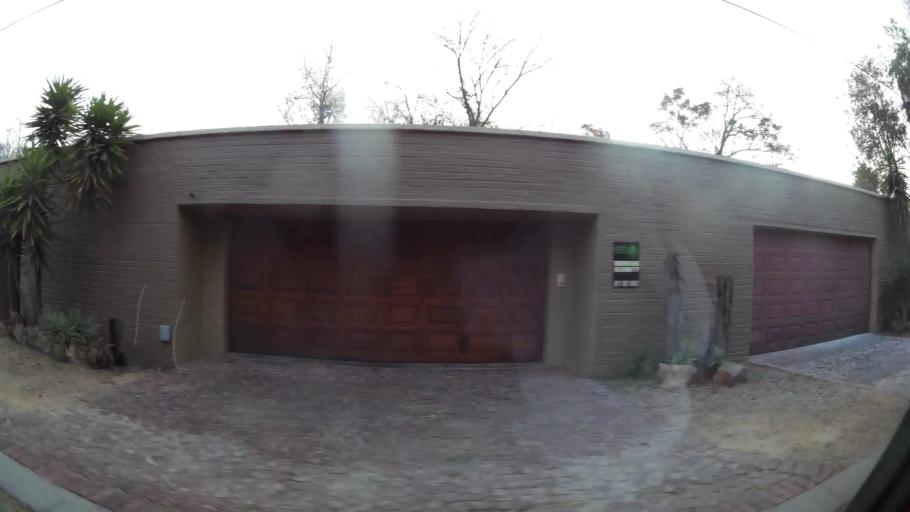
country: ZA
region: Gauteng
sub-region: City of Johannesburg Metropolitan Municipality
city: Diepsloot
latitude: -26.0403
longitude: 27.9862
